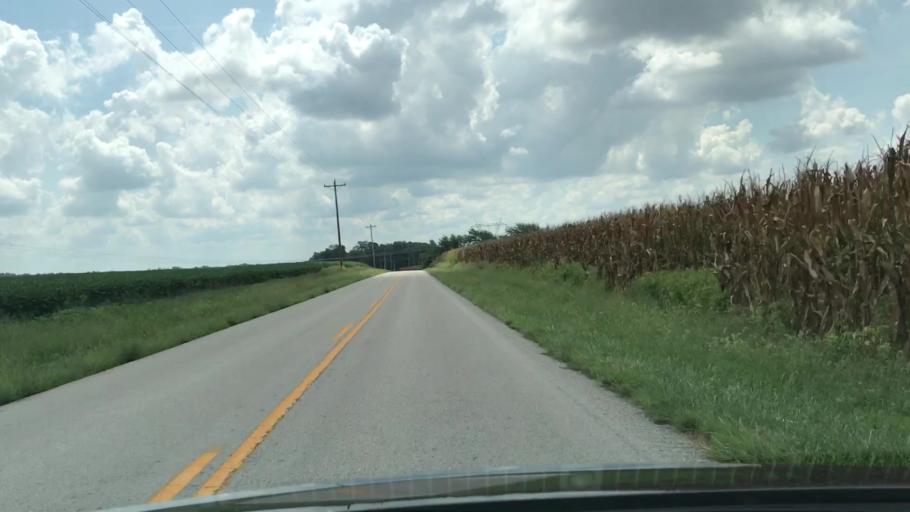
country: US
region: Kentucky
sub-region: Todd County
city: Elkton
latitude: 36.7767
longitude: -87.1194
